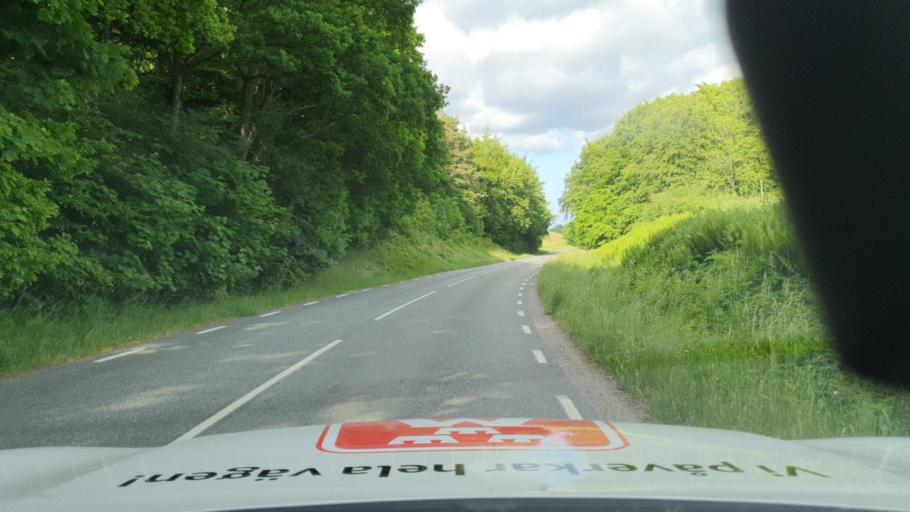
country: SE
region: Skane
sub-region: Simrishamns Kommun
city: Kivik
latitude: 55.6157
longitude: 14.2296
